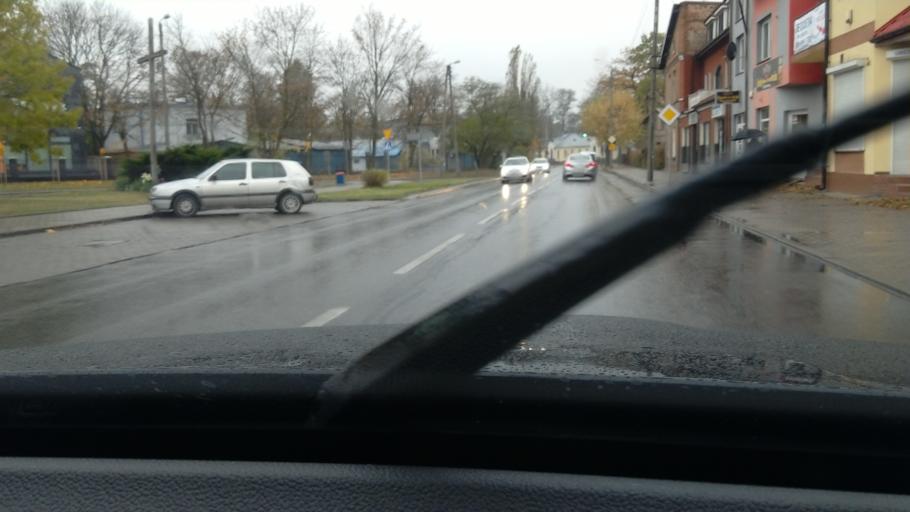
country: PL
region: Lodz Voivodeship
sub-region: Skierniewice
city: Skierniewice
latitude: 51.9626
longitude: 20.1482
